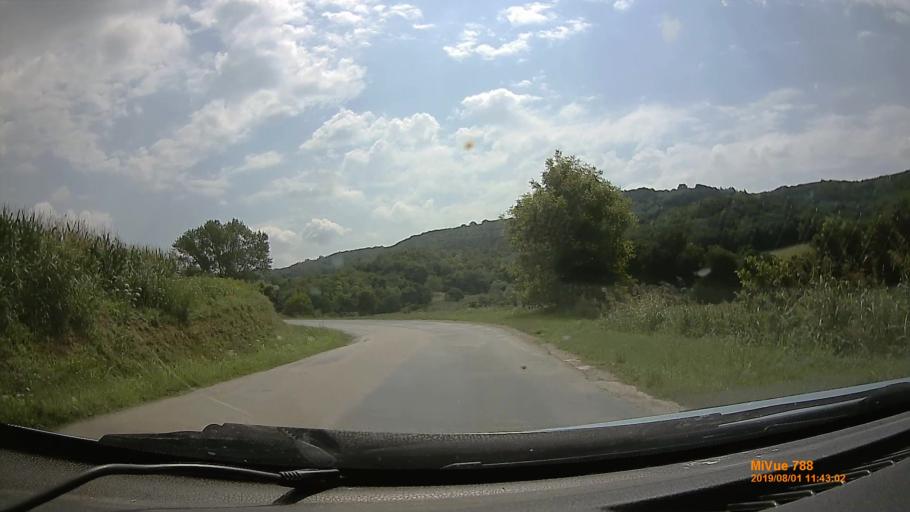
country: HU
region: Baranya
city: Villany
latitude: 45.8817
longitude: 18.4156
